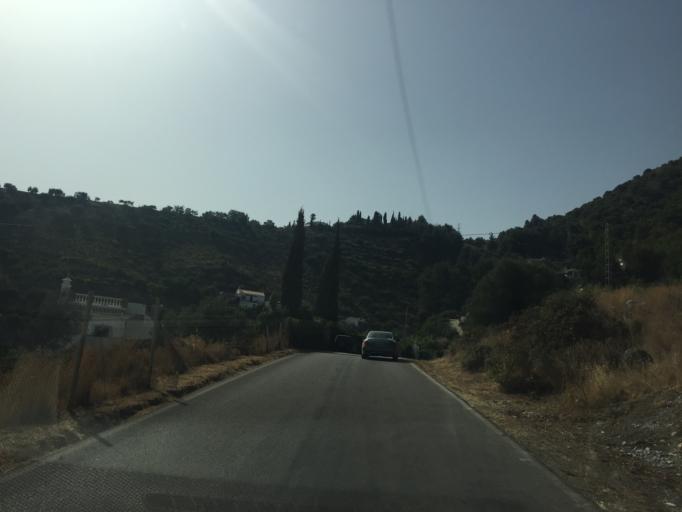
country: ES
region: Andalusia
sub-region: Provincia de Malaga
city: Frigiliana
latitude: 36.8042
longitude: -3.9152
